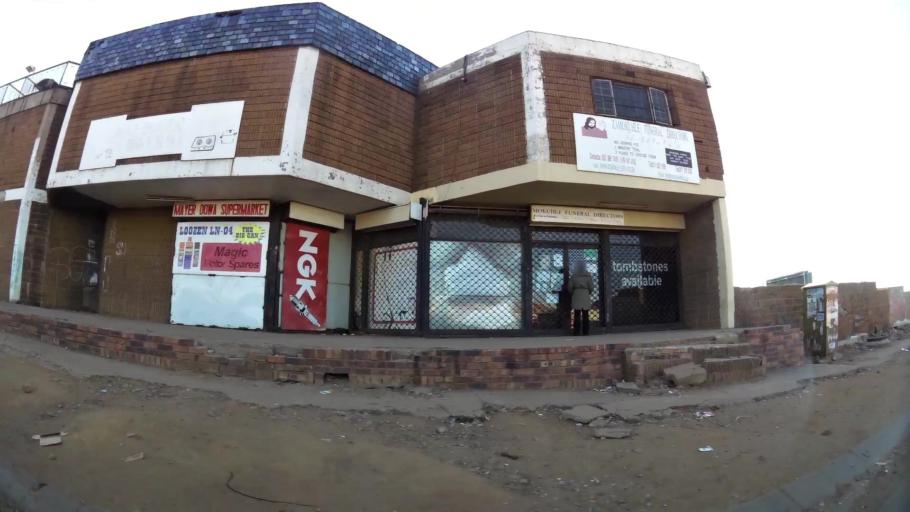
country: ZA
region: Gauteng
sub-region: Ekurhuleni Metropolitan Municipality
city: Tembisa
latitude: -26.0062
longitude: 28.2204
